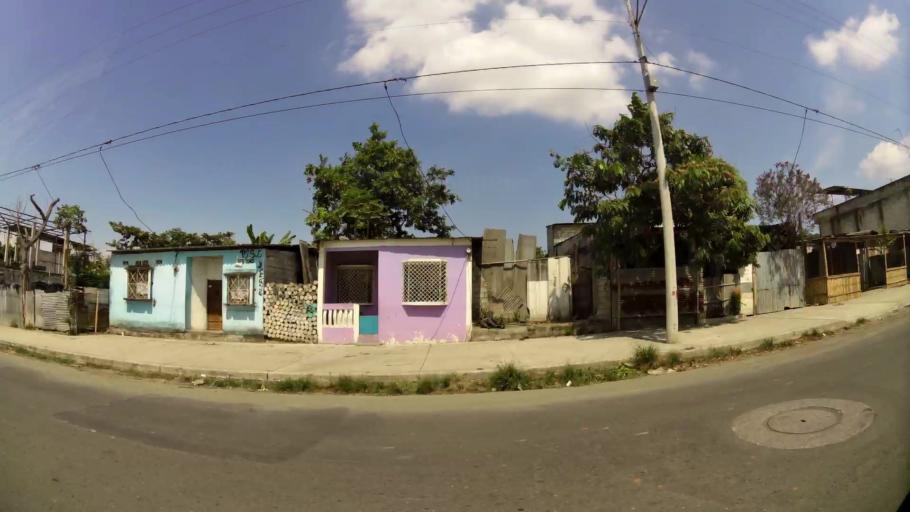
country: EC
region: Guayas
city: Eloy Alfaro
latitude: -2.1130
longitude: -79.9163
